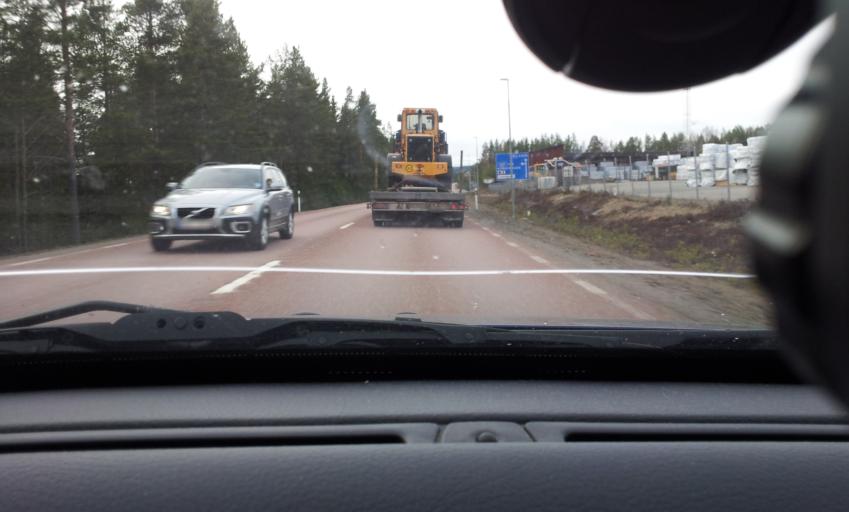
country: SE
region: Gaevleborg
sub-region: Ljusdals Kommun
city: Farila
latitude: 61.8052
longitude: 15.7800
